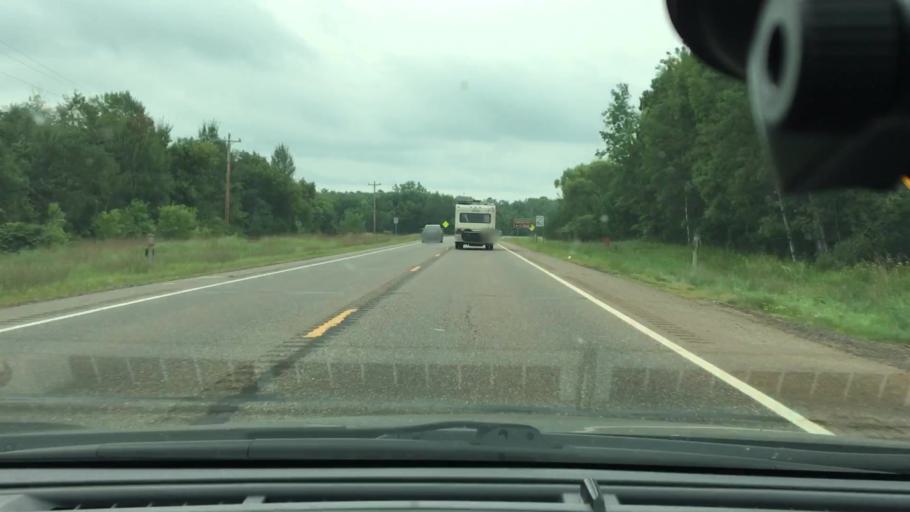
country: US
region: Minnesota
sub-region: Crow Wing County
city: Crosby
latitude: 46.4948
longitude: -93.9564
